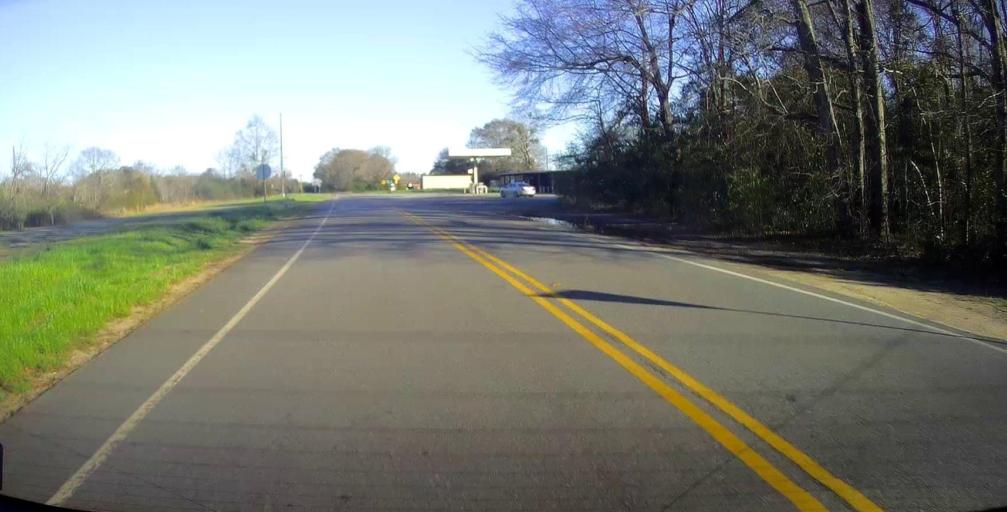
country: US
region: Georgia
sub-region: Taylor County
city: Butler
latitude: 32.5017
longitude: -84.4208
